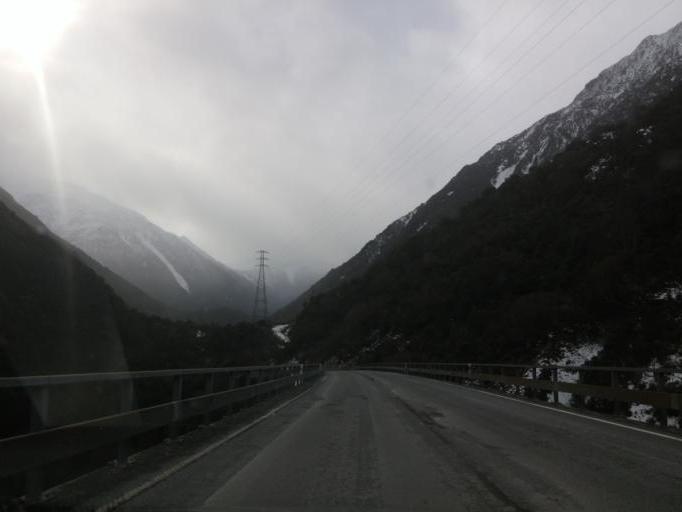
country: NZ
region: West Coast
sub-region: Grey District
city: Greymouth
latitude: -42.8854
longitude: 171.5558
